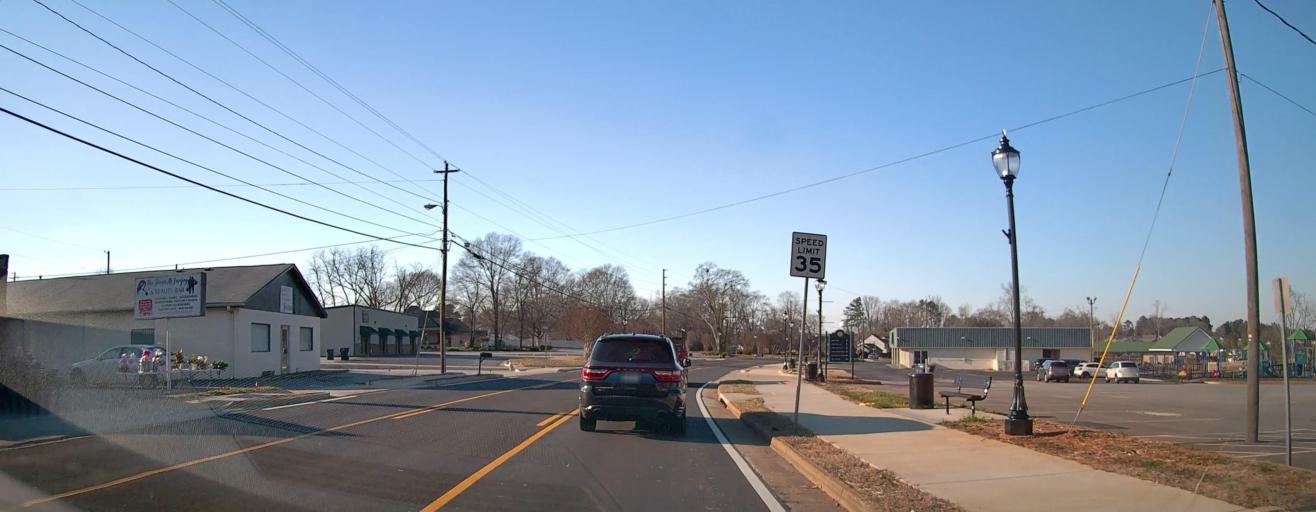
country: US
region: Georgia
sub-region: Clayton County
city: Lovejoy
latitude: 33.4369
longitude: -84.3140
